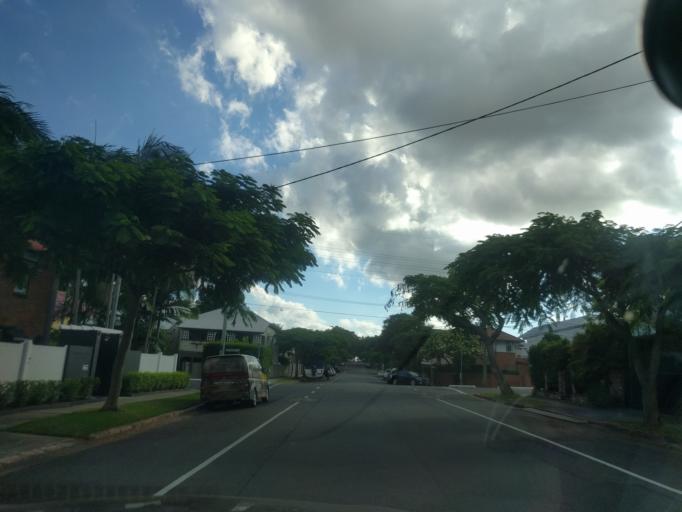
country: AU
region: Queensland
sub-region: Brisbane
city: Balmoral
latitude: -27.4692
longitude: 153.0474
